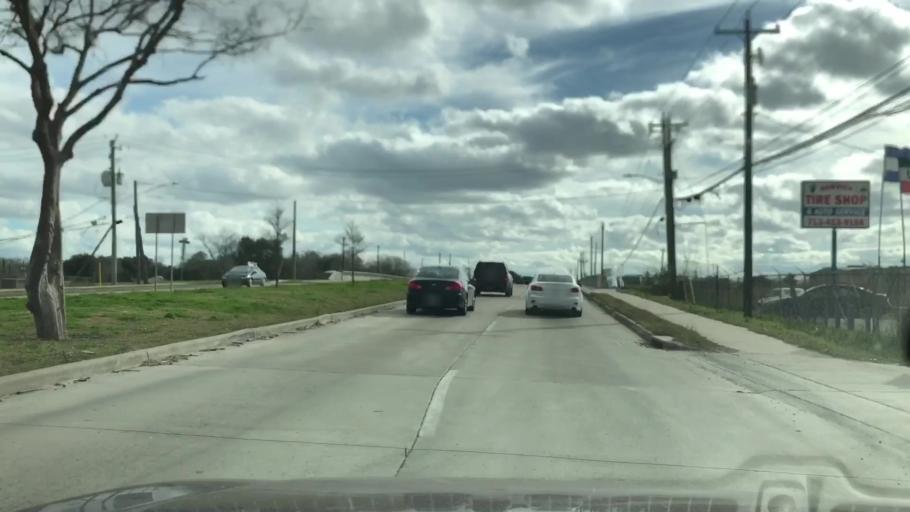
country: US
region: Texas
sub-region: Fort Bend County
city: Missouri City
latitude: 29.6210
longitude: -95.4652
